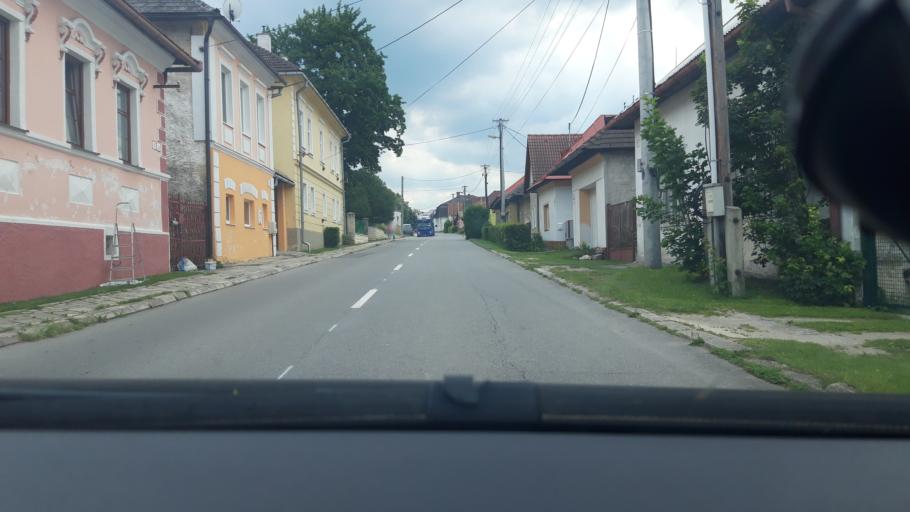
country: SK
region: Zilinsky
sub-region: Okres Martin
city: Martin
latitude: 48.9119
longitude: 18.8859
